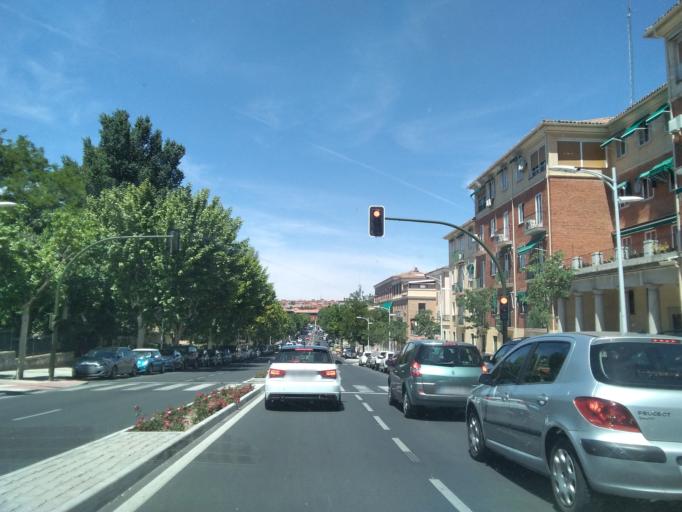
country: ES
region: Castille-La Mancha
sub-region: Province of Toledo
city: Toledo
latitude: 39.8631
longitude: -4.0275
